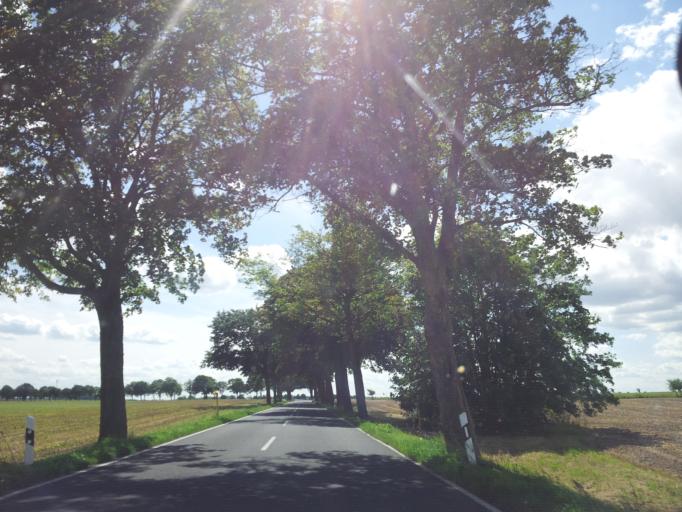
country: DE
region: Brandenburg
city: Niedergorsdorf
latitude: 52.0018
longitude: 12.9352
